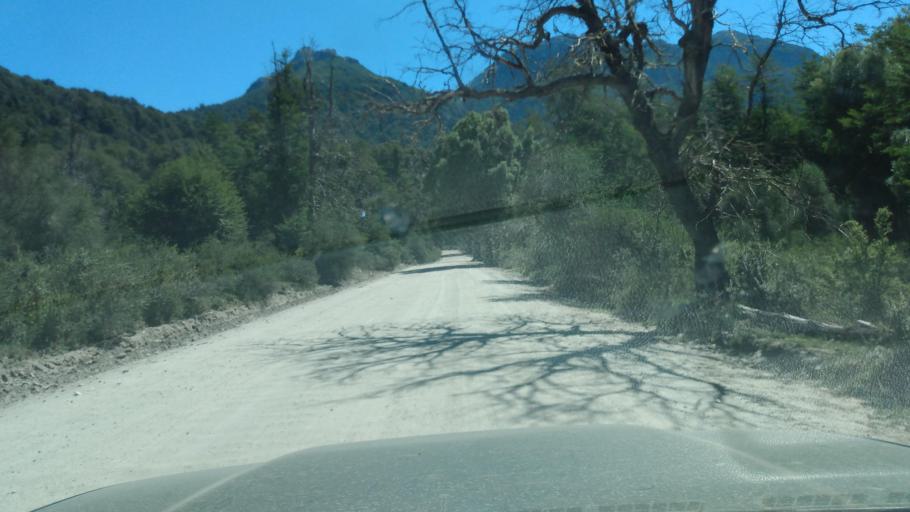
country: AR
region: Neuquen
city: Villa La Angostura
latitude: -40.6237
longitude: -71.5831
